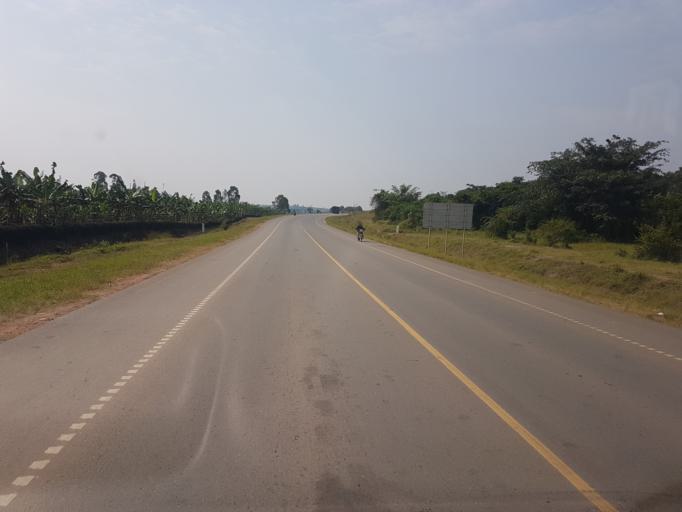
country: UG
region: Western Region
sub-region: Mbarara District
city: Bwizibwera
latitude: -0.6330
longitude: 30.5997
